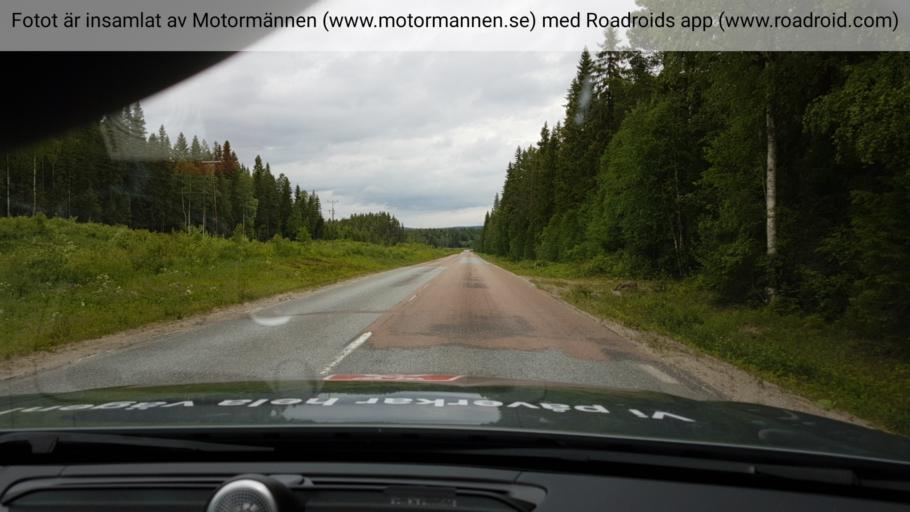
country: SE
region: Jaemtland
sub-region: Braecke Kommun
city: Braecke
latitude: 62.8783
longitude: 15.6040
